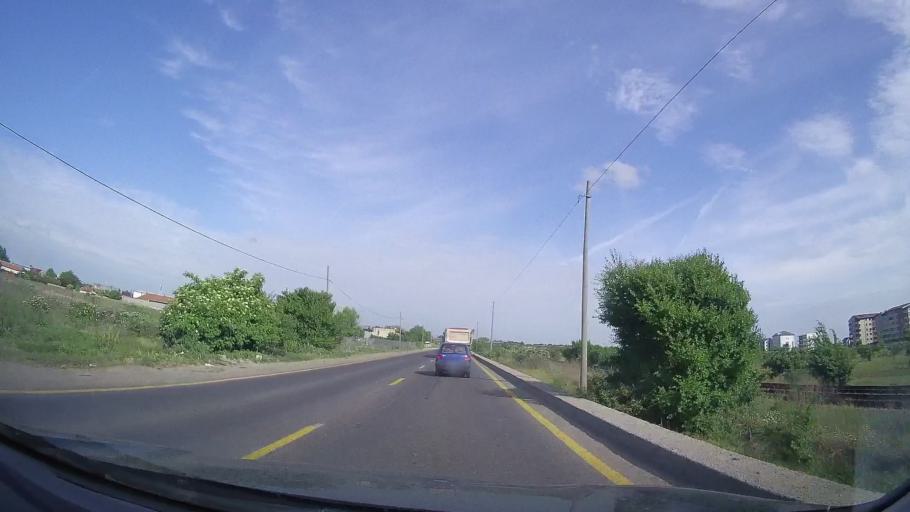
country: RO
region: Ilfov
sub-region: Comuna Bragadiru
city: Bragadiru
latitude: 44.3795
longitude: 25.9994
